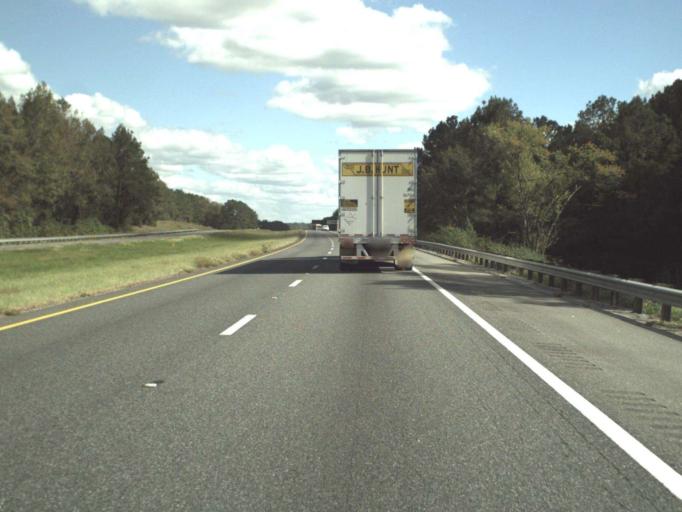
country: US
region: Florida
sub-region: Jackson County
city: Marianna
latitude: 30.7287
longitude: -85.2202
